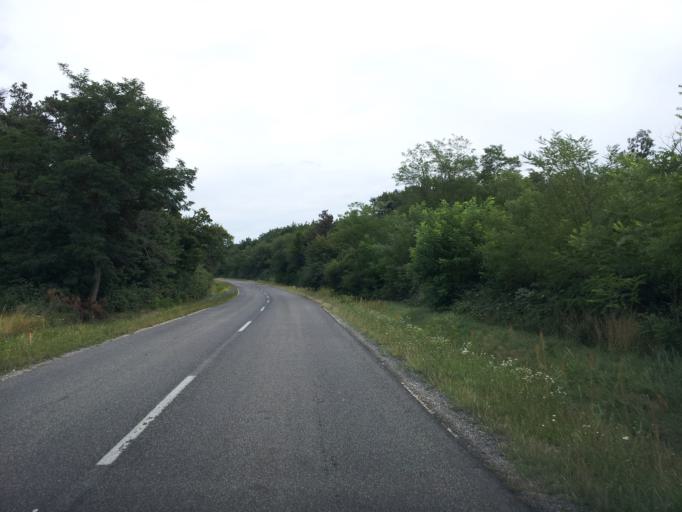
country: HU
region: Vas
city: Vasvar
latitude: 47.0474
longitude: 16.8300
